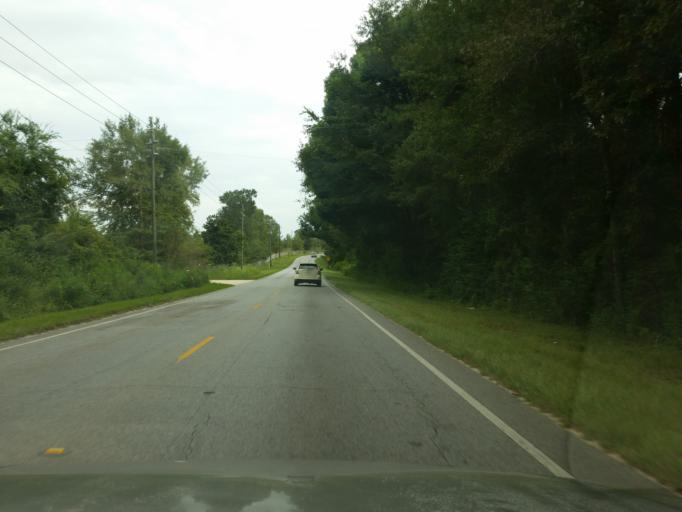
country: US
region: Florida
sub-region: Escambia County
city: Cantonment
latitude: 30.6485
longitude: -87.3196
